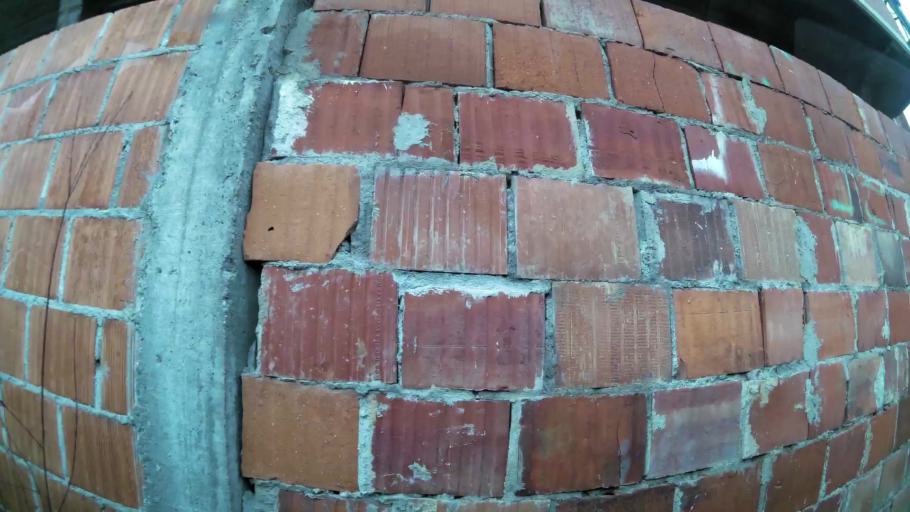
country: XK
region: Pristina
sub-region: Komuna e Prishtines
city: Pristina
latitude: 42.6800
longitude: 21.1715
